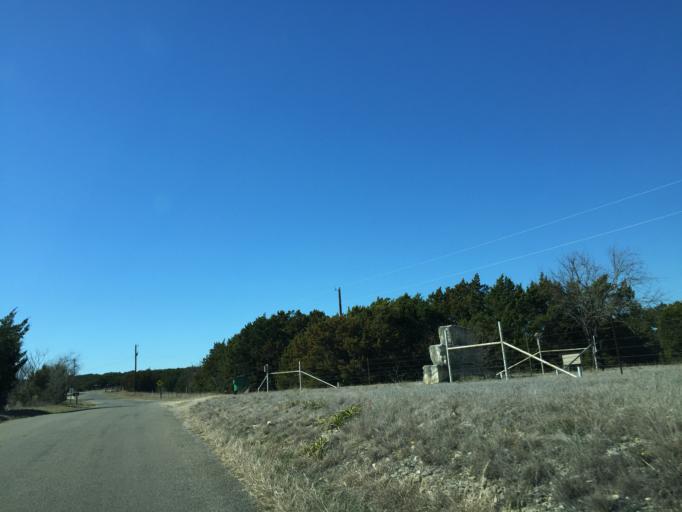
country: US
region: Texas
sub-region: Burnet County
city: Bertram
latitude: 30.9029
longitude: -98.1166
